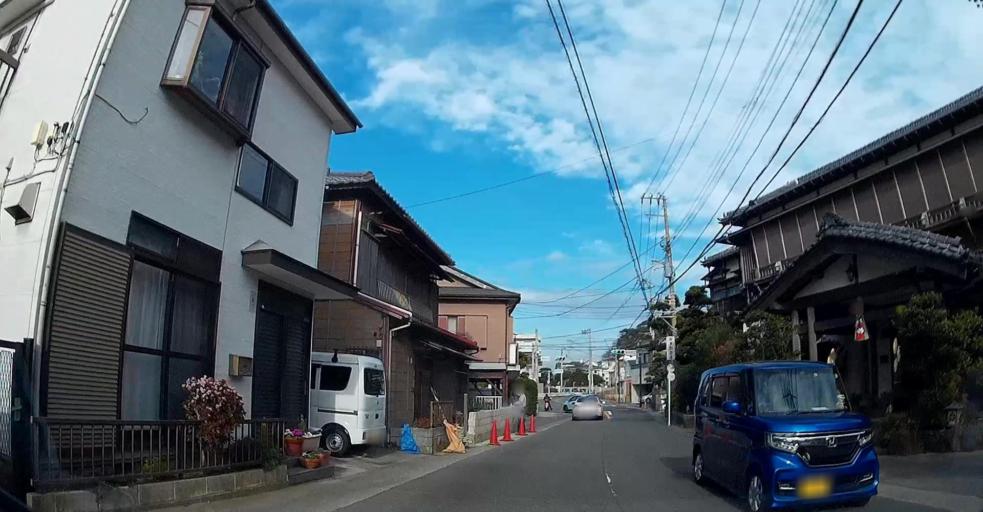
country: JP
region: Kanagawa
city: Hayama
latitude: 35.2841
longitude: 139.5697
